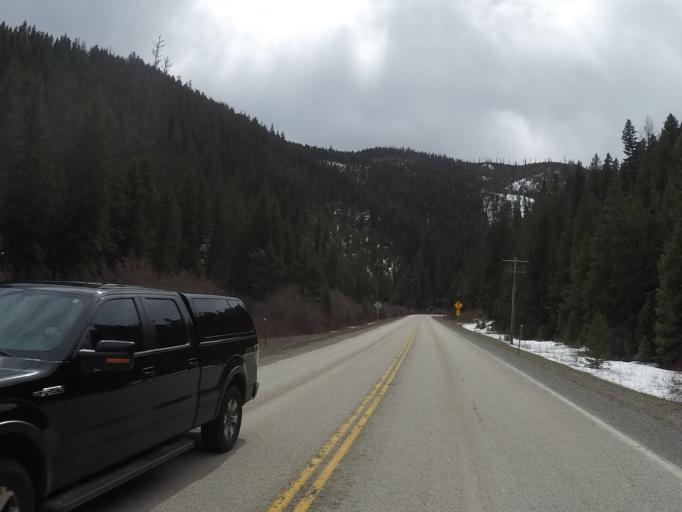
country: US
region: Montana
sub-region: Missoula County
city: Frenchtown
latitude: 46.7633
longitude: -114.4851
